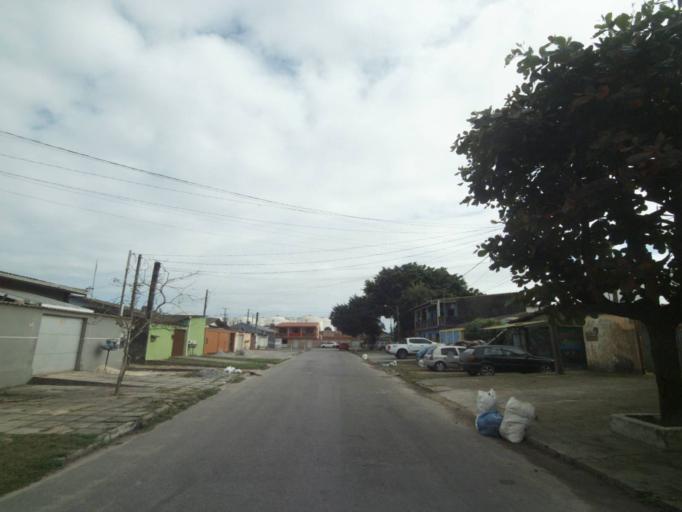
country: BR
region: Parana
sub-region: Paranagua
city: Paranagua
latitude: -25.5142
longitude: -48.5302
